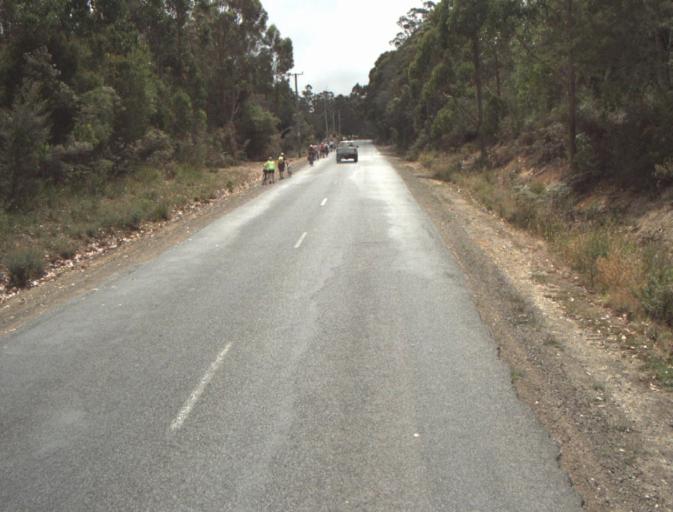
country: AU
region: Tasmania
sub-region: Launceston
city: Mayfield
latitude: -41.2183
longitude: 147.2082
